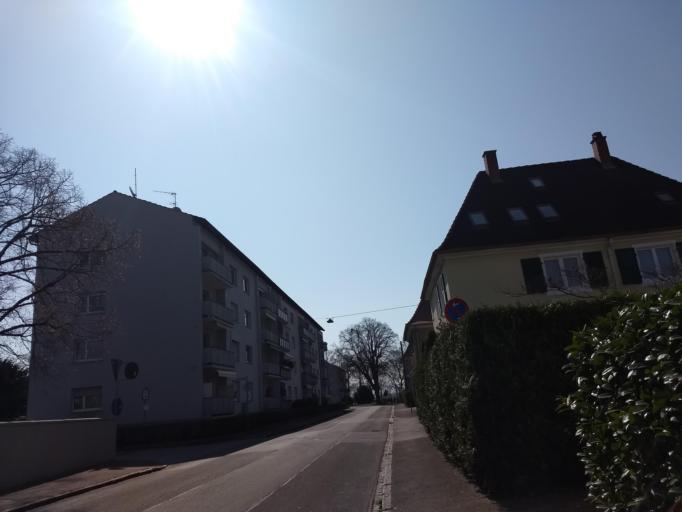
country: DE
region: Baden-Wuerttemberg
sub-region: Freiburg Region
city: Weil am Rhein
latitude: 47.5906
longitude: 7.6207
